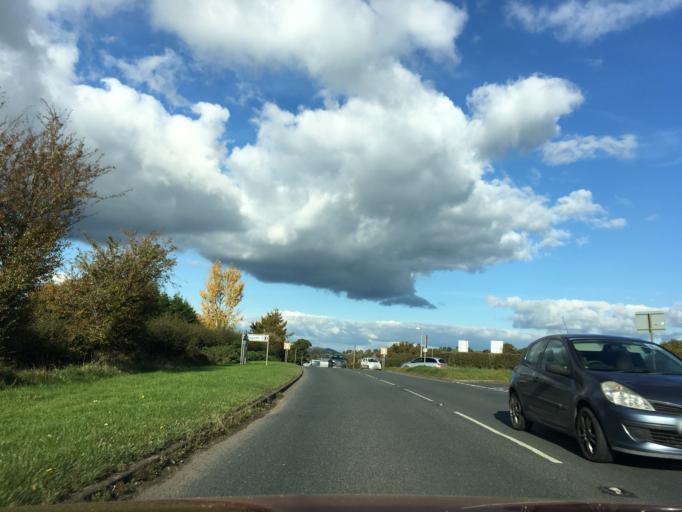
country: GB
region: Wales
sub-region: Sir Powys
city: Hay
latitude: 52.0244
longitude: -3.2159
